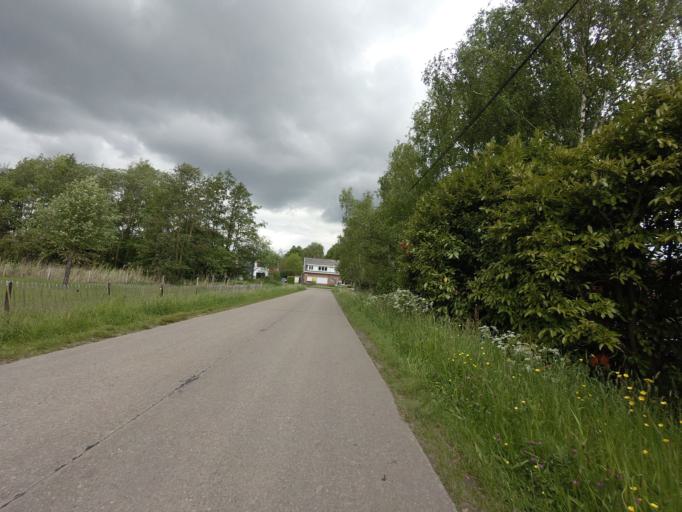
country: BE
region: Flanders
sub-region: Provincie Antwerpen
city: Mechelen
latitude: 51.0665
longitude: 4.4695
